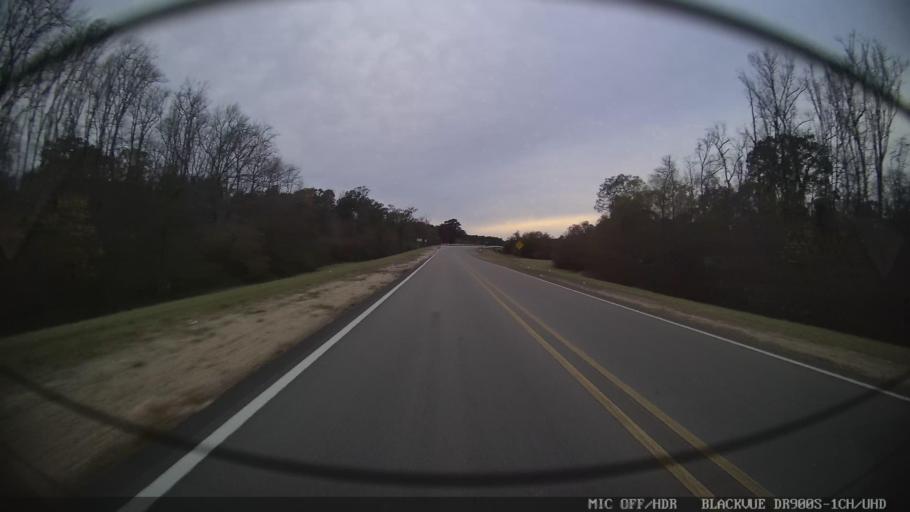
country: US
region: Mississippi
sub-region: Clarke County
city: Quitman
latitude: 32.0420
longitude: -88.7410
